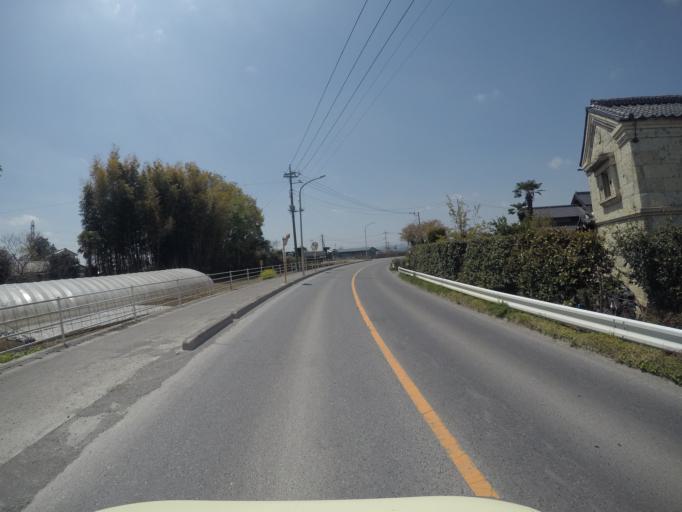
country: JP
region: Tochigi
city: Mibu
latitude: 36.4339
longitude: 139.7665
